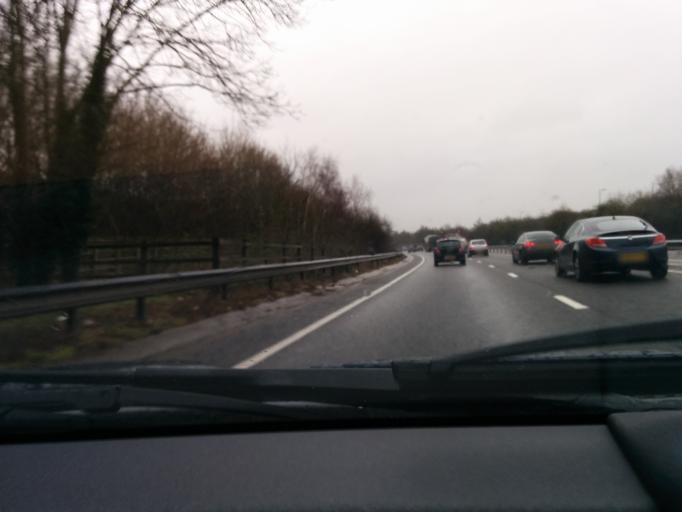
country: GB
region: England
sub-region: Oxfordshire
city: Abingdon
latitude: 51.6788
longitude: -1.2993
